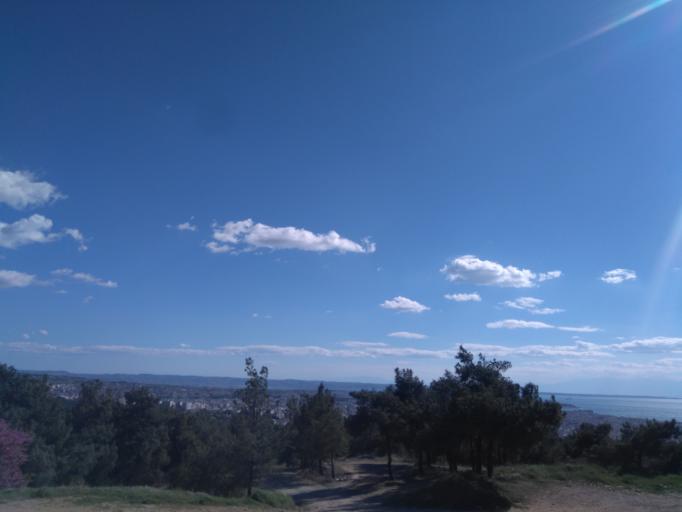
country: GR
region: Central Macedonia
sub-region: Nomos Thessalonikis
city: Triandria
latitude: 40.6310
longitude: 22.9786
